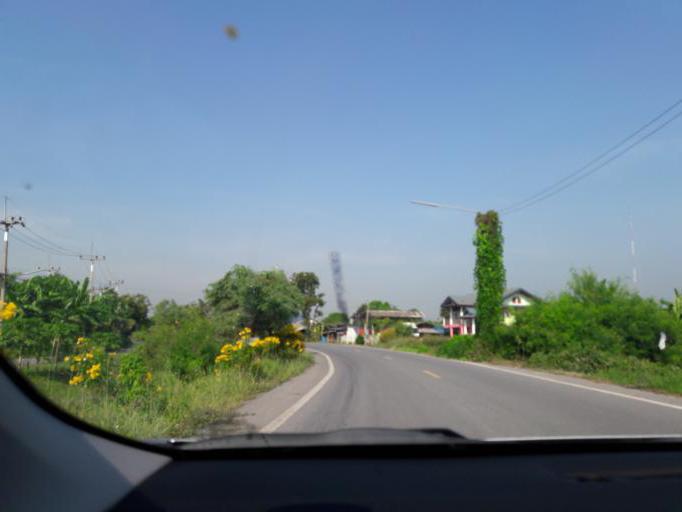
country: TH
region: Ang Thong
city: Ang Thong
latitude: 14.5871
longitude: 100.4355
